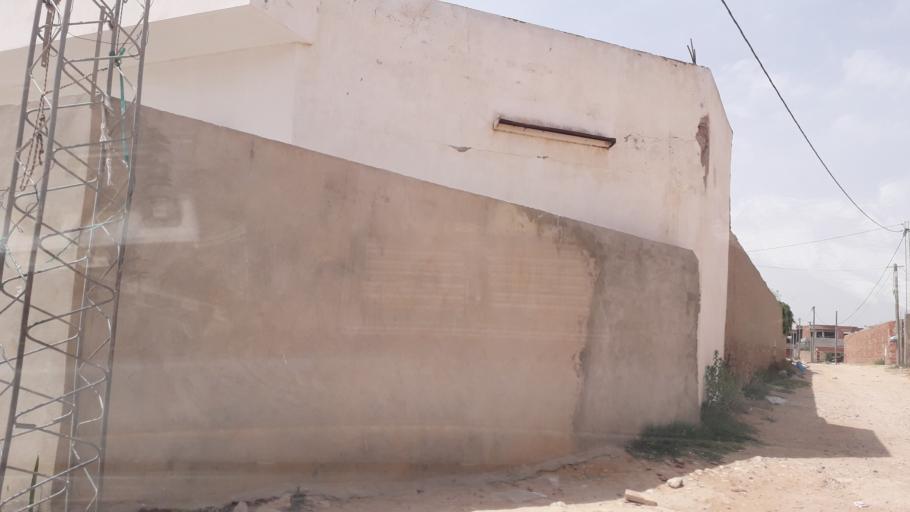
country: TN
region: Safaqis
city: Al Qarmadah
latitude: 34.8446
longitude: 10.7774
